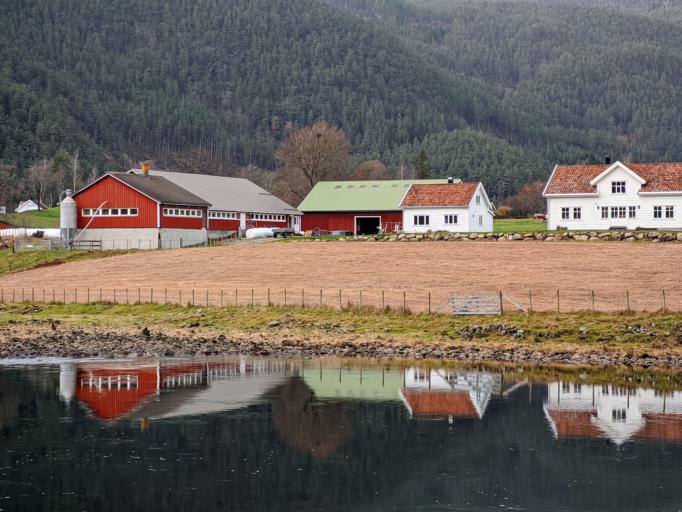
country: NO
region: Rogaland
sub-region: Suldal
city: Sand
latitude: 59.4629
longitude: 6.4249
